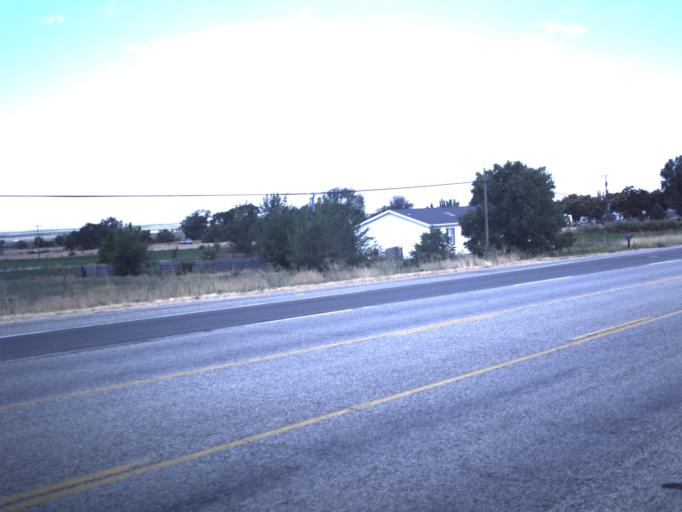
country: US
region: Utah
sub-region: Box Elder County
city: Willard
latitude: 41.4207
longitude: -112.0358
